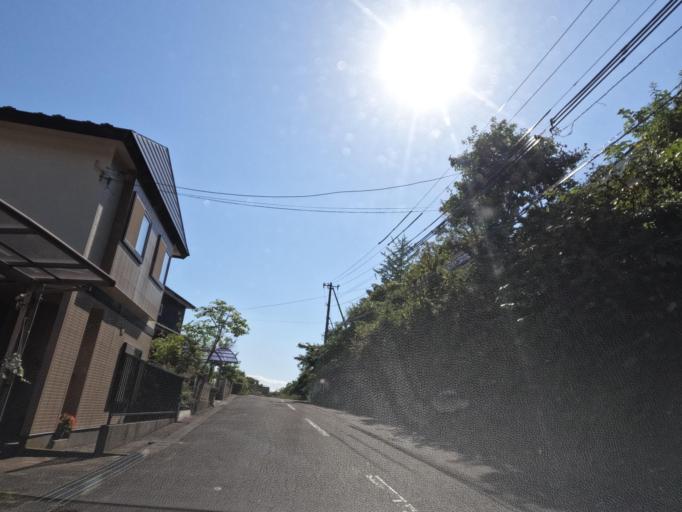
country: JP
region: Hokkaido
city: Muroran
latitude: 42.3700
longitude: 141.0251
